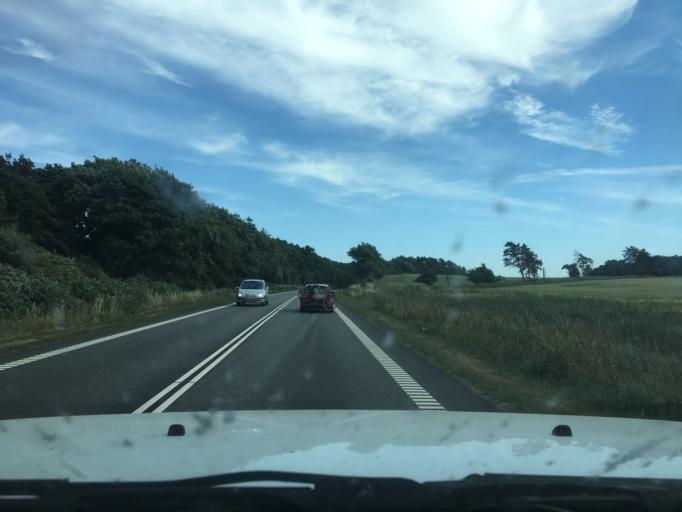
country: DK
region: Central Jutland
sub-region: Viborg Kommune
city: Viborg
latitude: 56.5485
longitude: 9.3971
